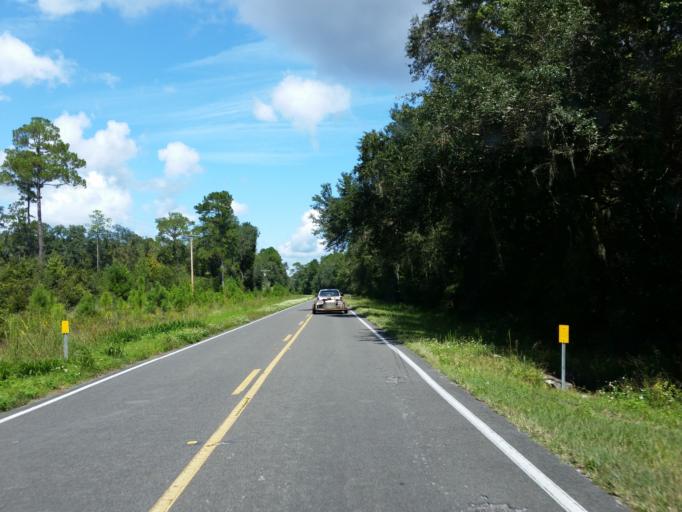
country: US
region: Florida
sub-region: Alachua County
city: Gainesville
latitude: 29.5360
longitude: -82.2685
